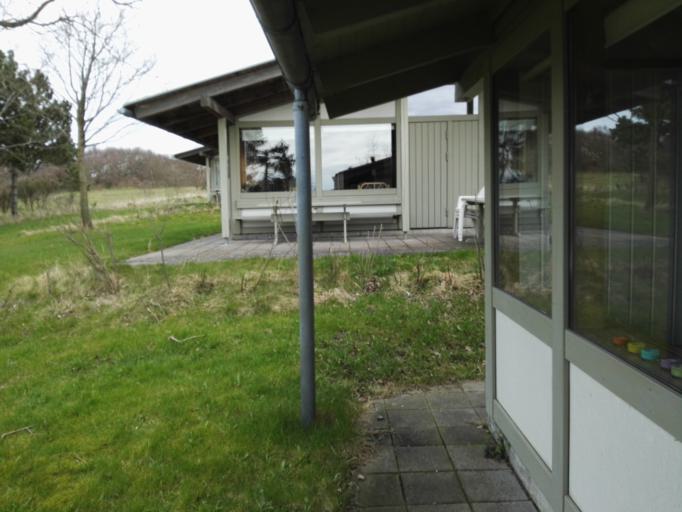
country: DK
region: Capital Region
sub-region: Gribskov Kommune
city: Gilleleje
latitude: 56.1250
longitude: 12.2675
